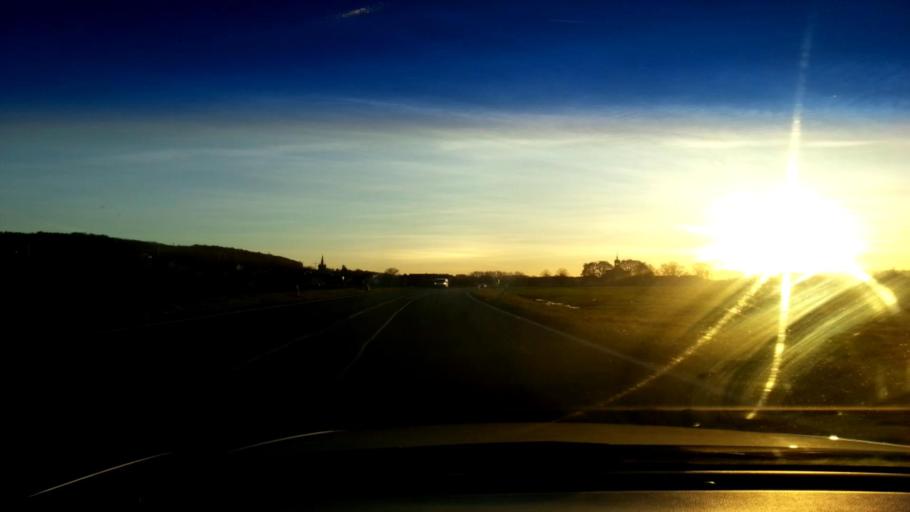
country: DE
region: Bavaria
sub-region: Upper Franconia
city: Ebensfeld
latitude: 50.0441
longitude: 10.9504
